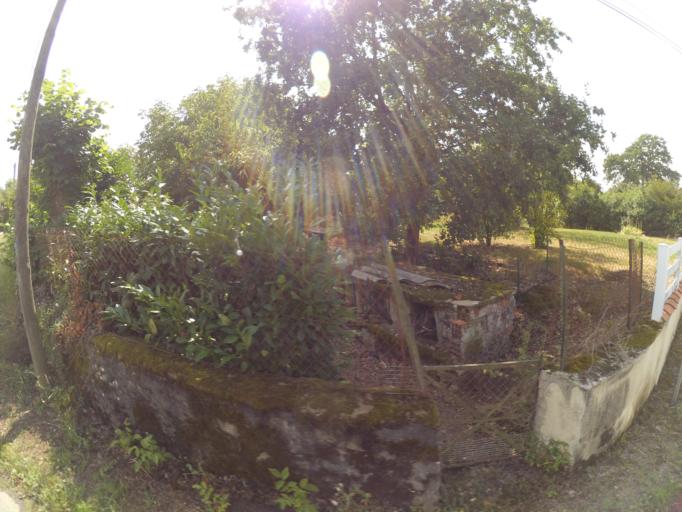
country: FR
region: Pays de la Loire
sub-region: Departement de la Vendee
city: La Bernardiere
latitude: 47.0216
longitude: -1.2639
